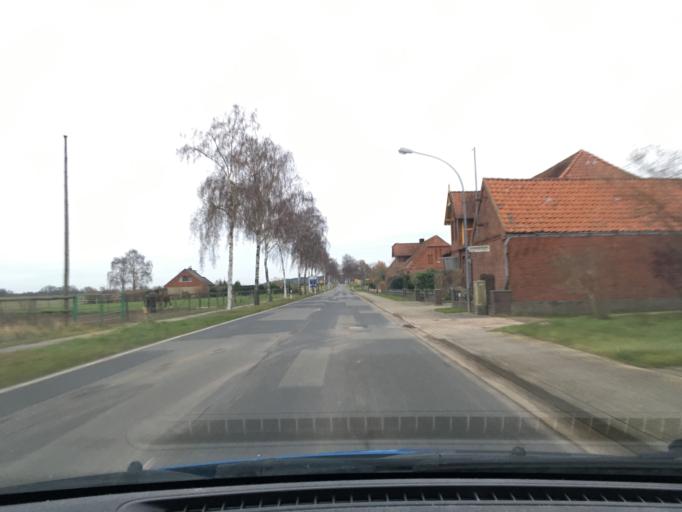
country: DE
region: Lower Saxony
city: Neu Darchau
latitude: 53.2380
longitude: 10.8527
